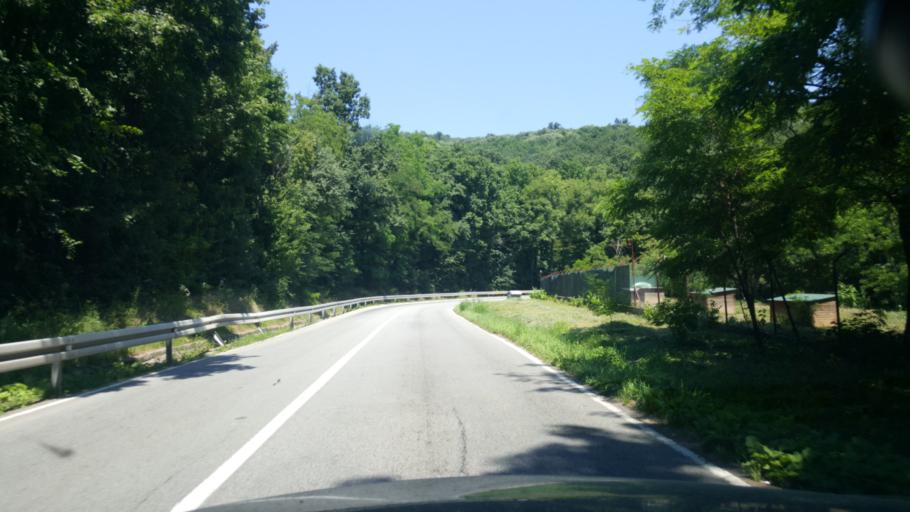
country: RS
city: Rusanj
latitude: 44.6856
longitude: 20.5088
